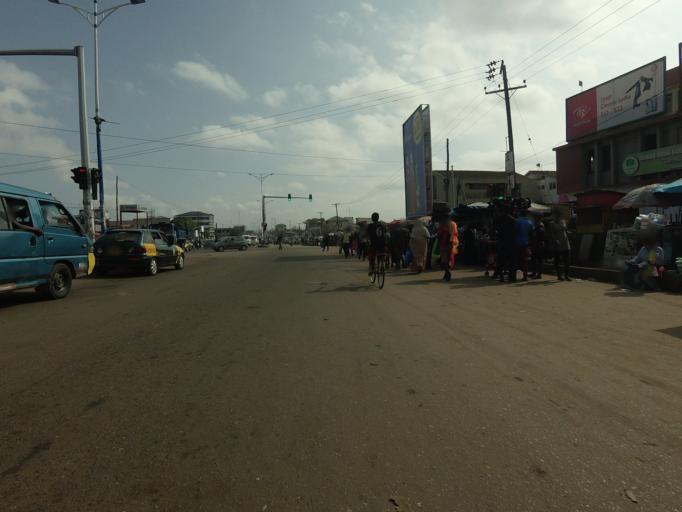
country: GH
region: Greater Accra
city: Tema
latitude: 5.6883
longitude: -0.0300
